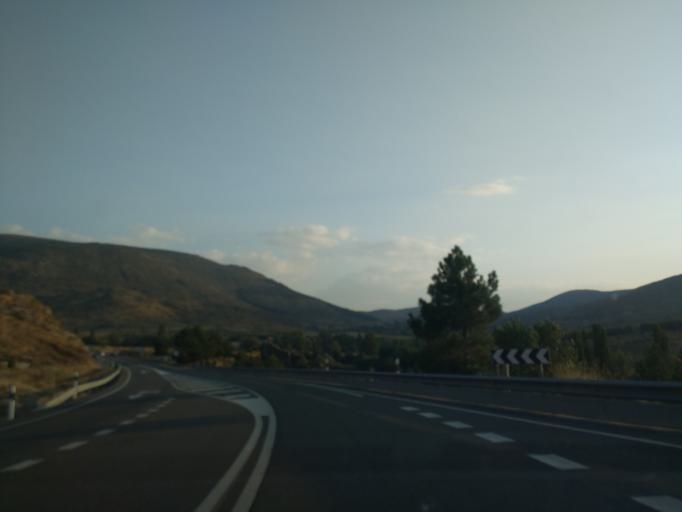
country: ES
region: Castille and Leon
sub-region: Provincia de Avila
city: Mengamunoz
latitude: 40.5187
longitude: -4.9863
